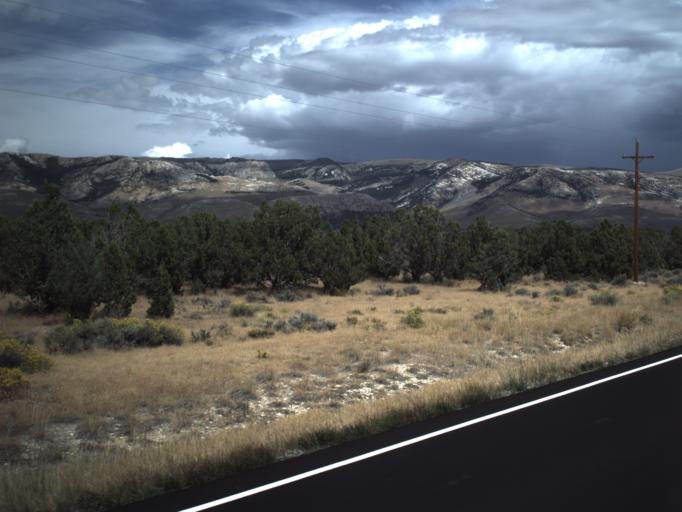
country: US
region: Idaho
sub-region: Cassia County
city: Burley
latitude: 41.8120
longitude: -113.4408
